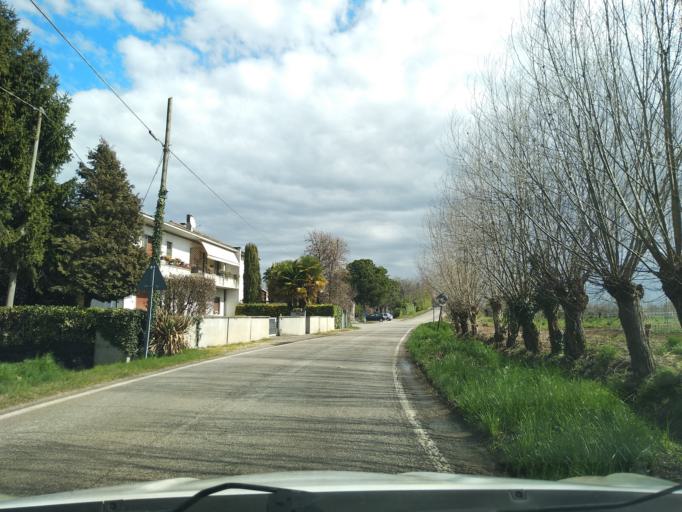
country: IT
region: Veneto
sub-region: Provincia di Vicenza
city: Vigardolo
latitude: 45.6109
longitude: 11.5960
